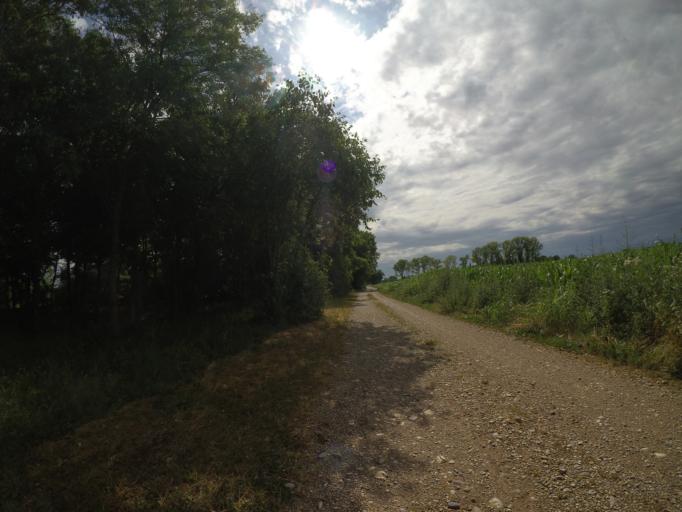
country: IT
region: Friuli Venezia Giulia
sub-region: Provincia di Udine
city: Lestizza
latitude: 45.9668
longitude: 13.1347
